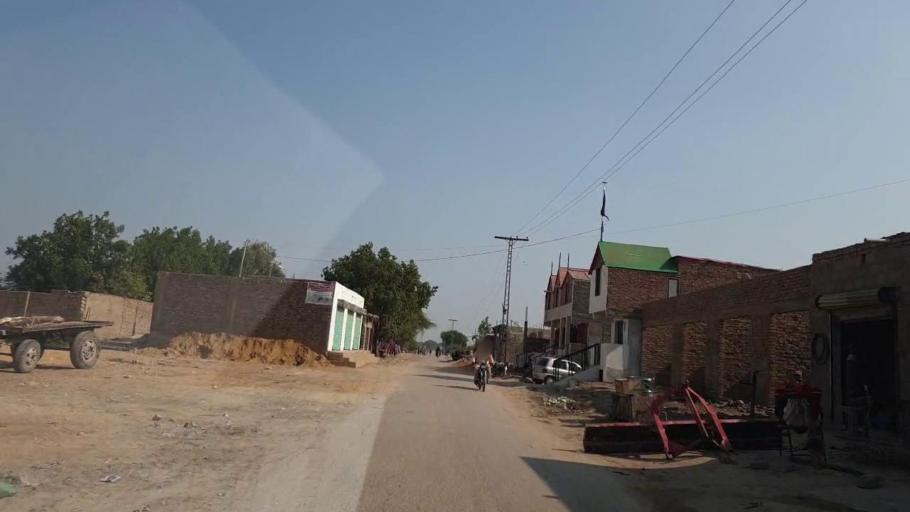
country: PK
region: Sindh
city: Matiari
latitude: 25.5029
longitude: 68.4362
